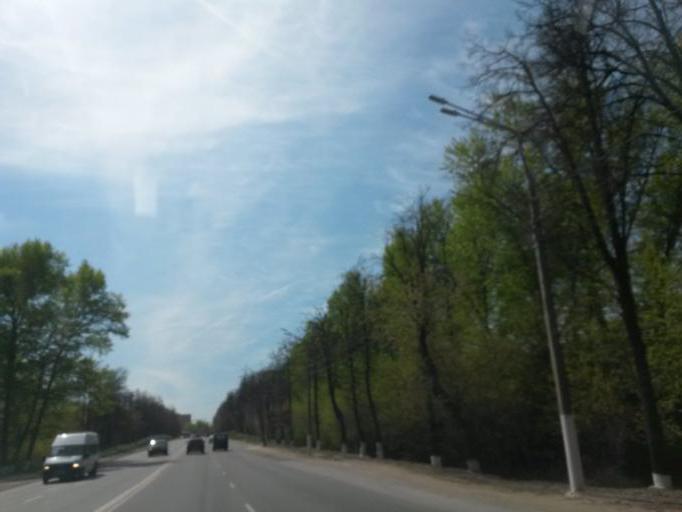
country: RU
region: Moskovskaya
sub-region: Podol'skiy Rayon
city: Podol'sk
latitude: 55.4556
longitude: 37.5555
